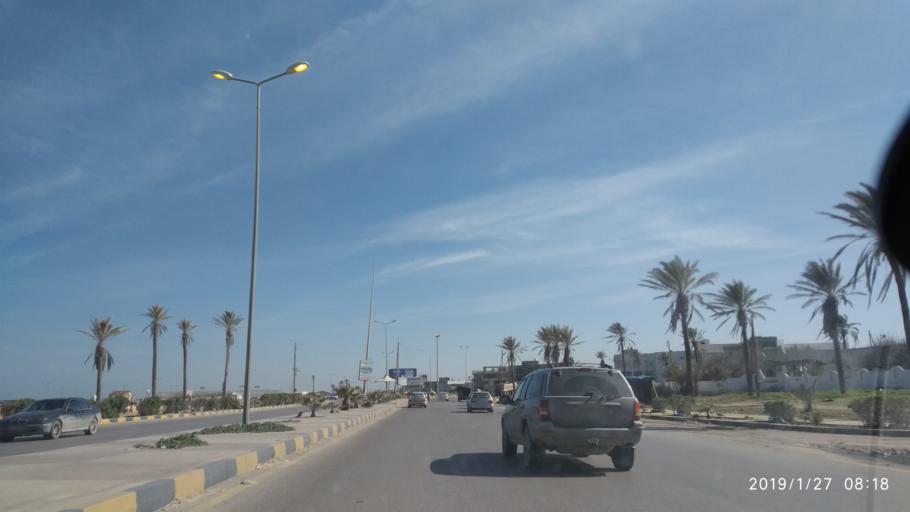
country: LY
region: Tripoli
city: Tagiura
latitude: 32.8945
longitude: 13.3411
